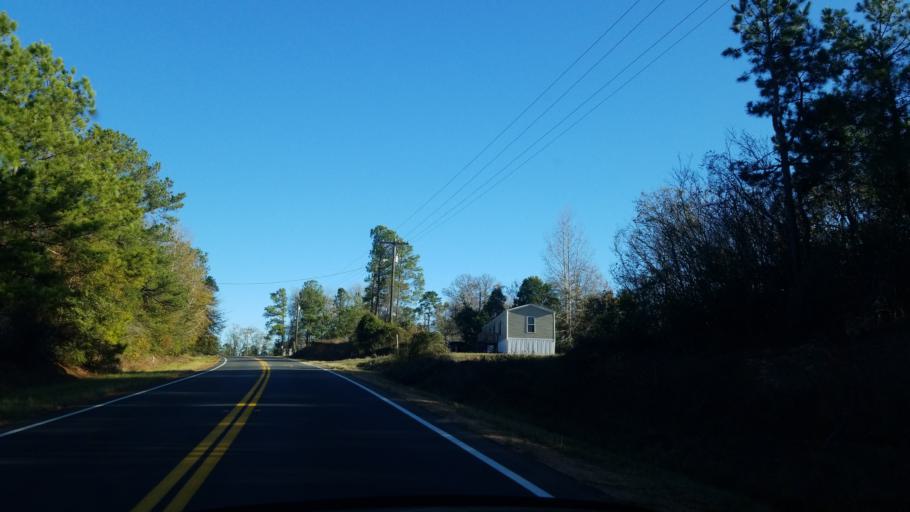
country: US
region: Georgia
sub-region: Talbot County
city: Talbotton
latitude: 32.5774
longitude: -84.5468
